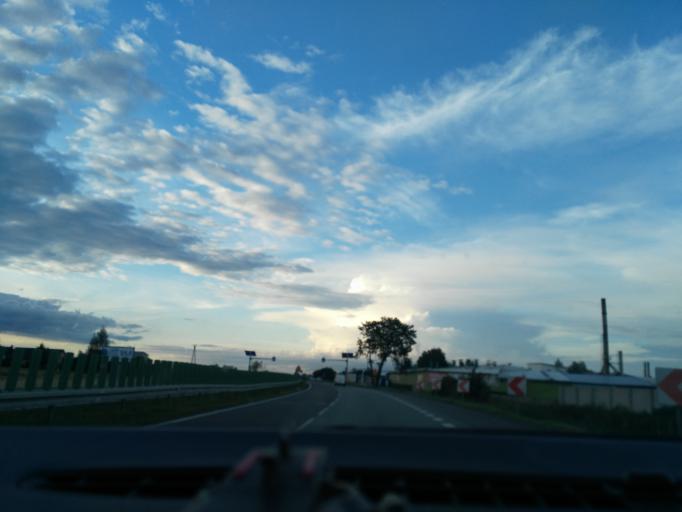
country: PL
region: Lublin Voivodeship
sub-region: Powiat lubelski
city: Niemce
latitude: 51.3360
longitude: 22.6177
